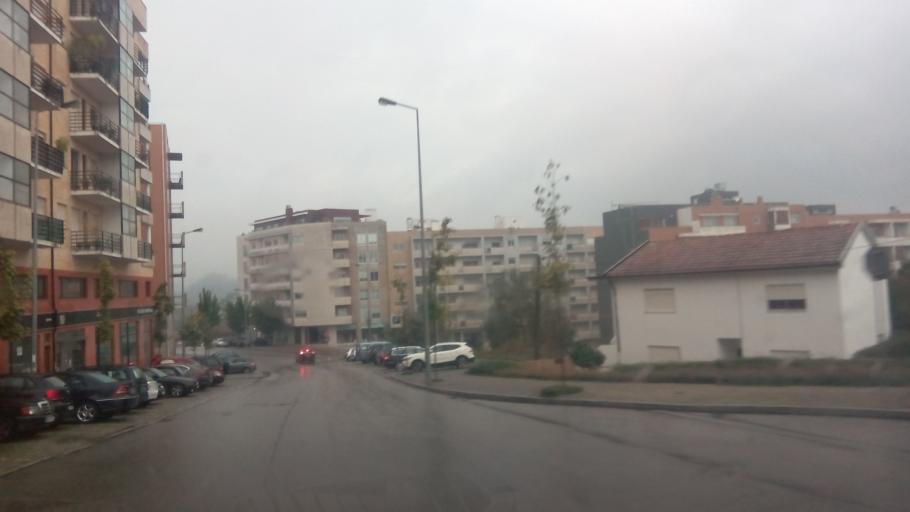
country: PT
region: Porto
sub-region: Paredes
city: Paredes
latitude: 41.2083
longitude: -8.3311
